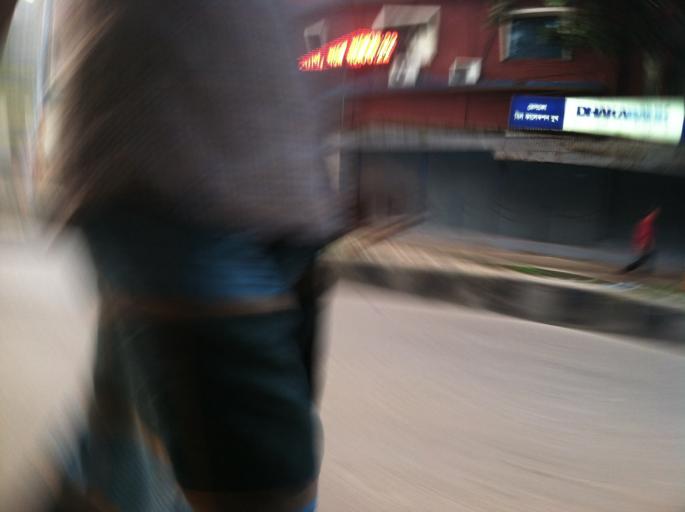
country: BD
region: Dhaka
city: Paltan
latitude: 23.7803
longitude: 90.4168
